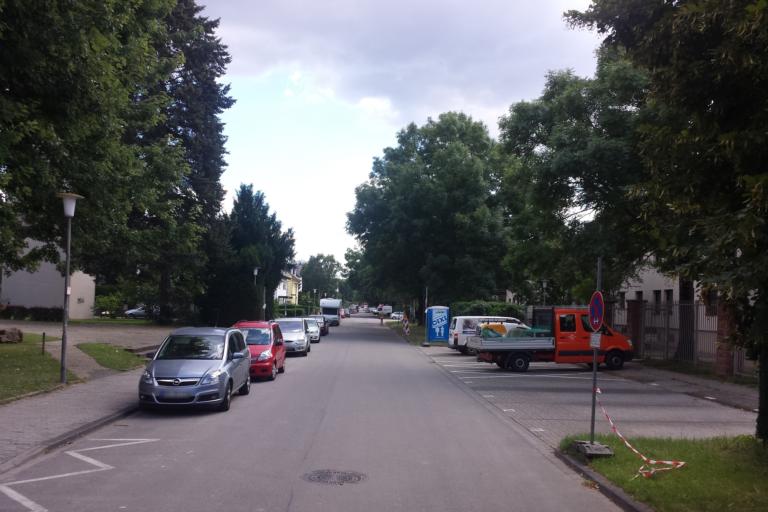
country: DE
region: Baden-Wuerttemberg
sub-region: Karlsruhe Region
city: Heidelberg
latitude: 49.3884
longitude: 8.6876
